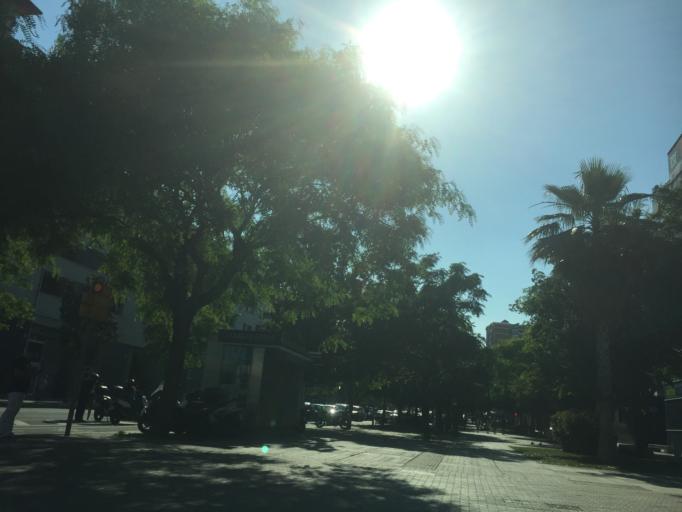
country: ES
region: Catalonia
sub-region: Provincia de Barcelona
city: Sant Marti
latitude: 41.4228
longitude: 2.1911
